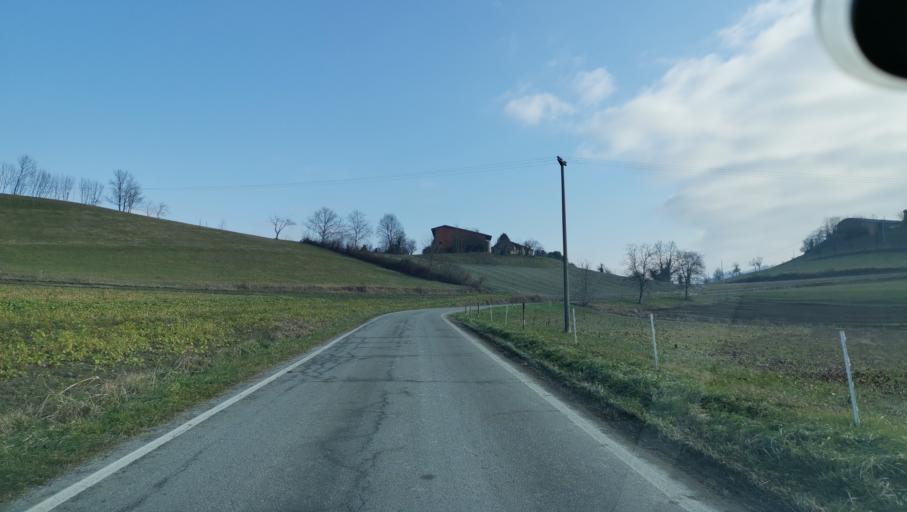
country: IT
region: Piedmont
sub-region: Provincia di Torino
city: Rivalba
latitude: 45.1056
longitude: 7.8887
